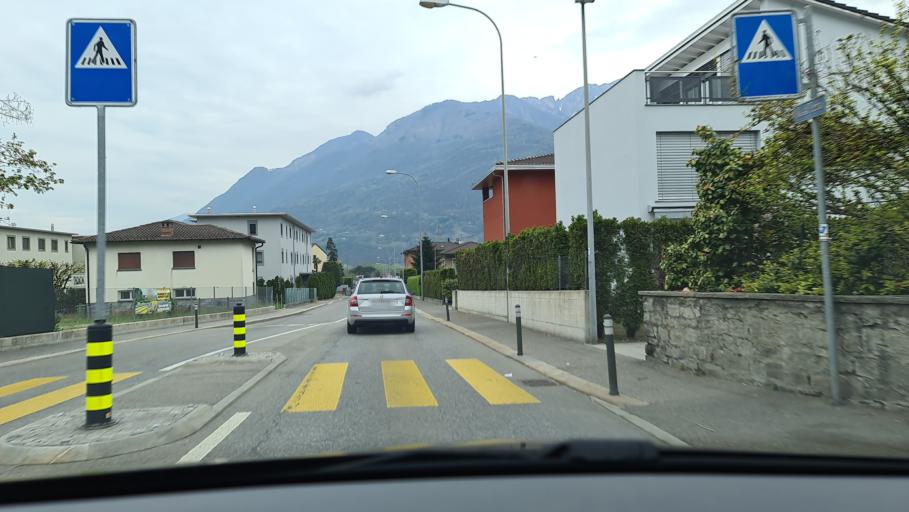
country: CH
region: Ticino
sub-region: Bellinzona District
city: Giubiasco
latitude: 46.1716
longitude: 9.0058
